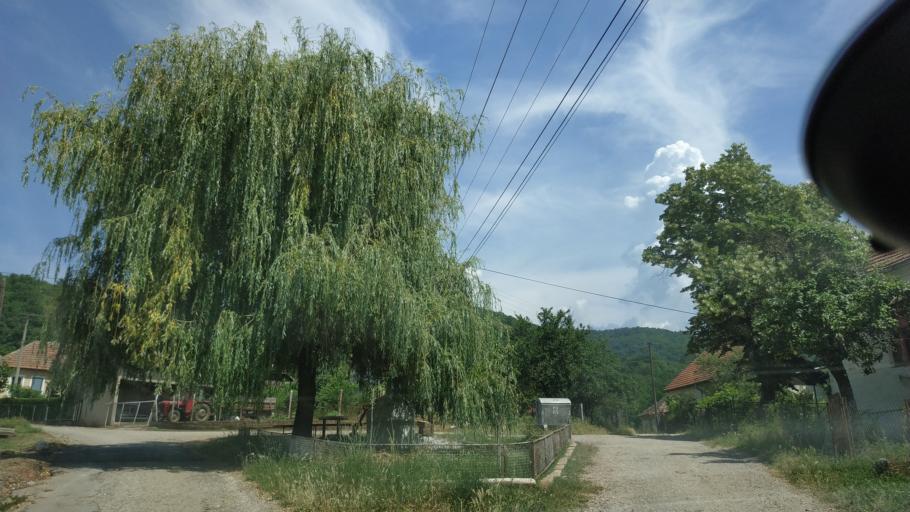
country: RS
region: Central Serbia
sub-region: Nisavski Okrug
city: Aleksinac
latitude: 43.5988
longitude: 21.6973
